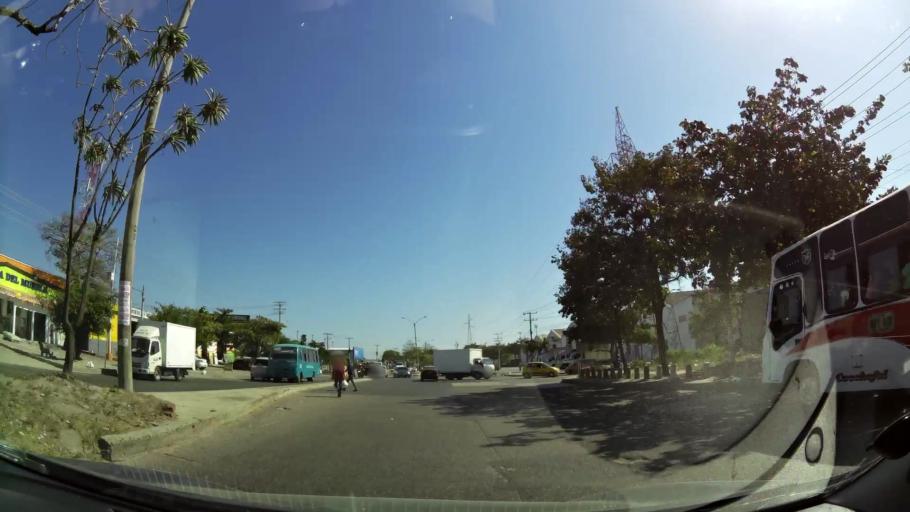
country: CO
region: Atlantico
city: Barranquilla
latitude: 10.9485
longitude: -74.7853
